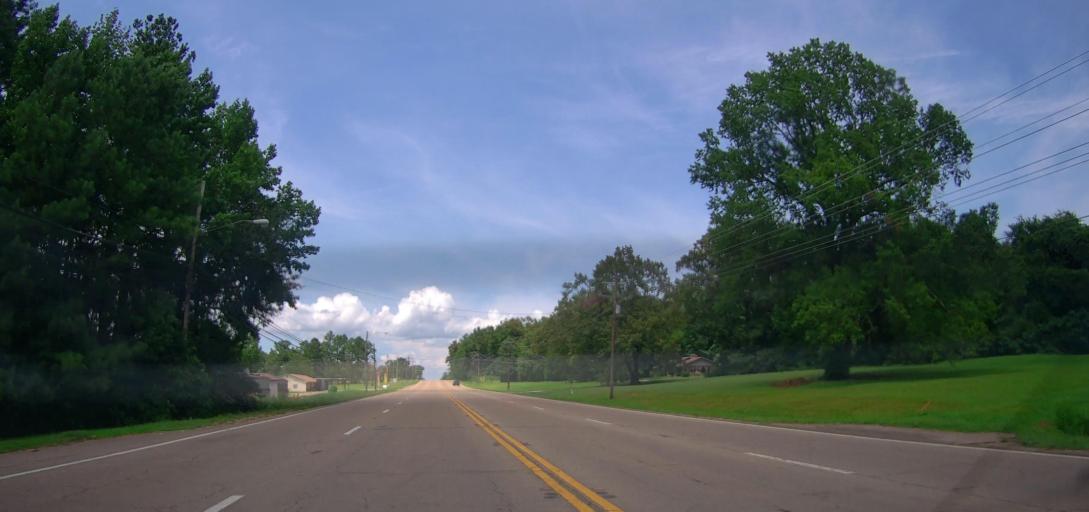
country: US
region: Mississippi
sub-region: Lee County
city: Verona
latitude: 34.1711
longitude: -88.7197
